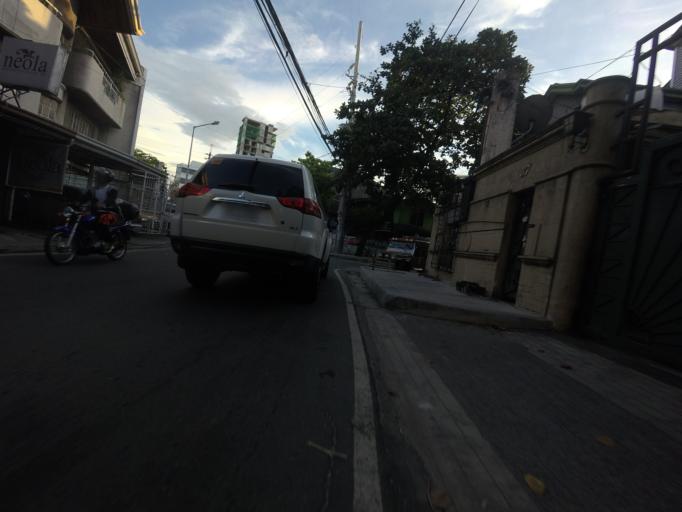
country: PH
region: Metro Manila
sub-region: San Juan
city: San Juan
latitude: 14.6001
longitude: 121.0377
